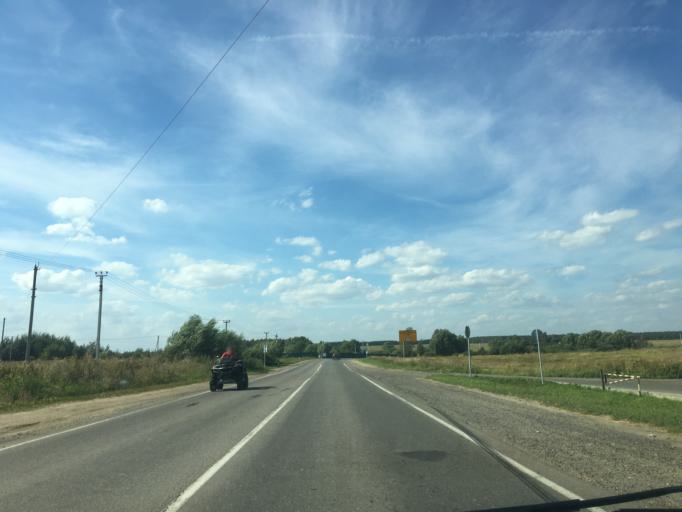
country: RU
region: Moskovskaya
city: Yam
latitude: 55.4771
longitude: 37.6658
